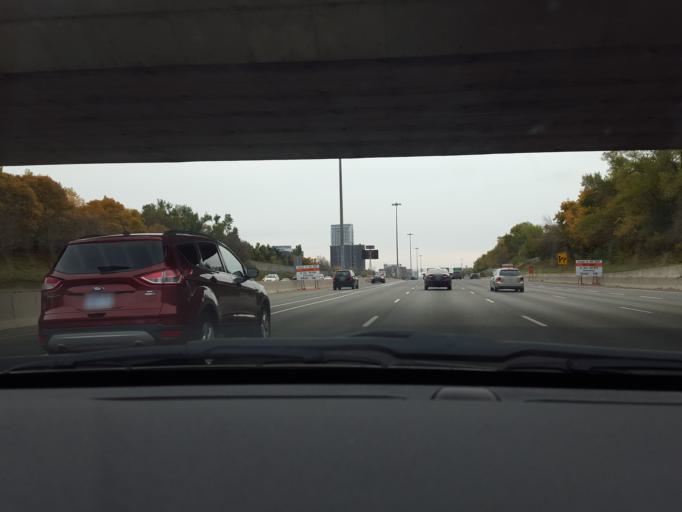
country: CA
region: Ontario
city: Willowdale
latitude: 43.7868
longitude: -79.3420
